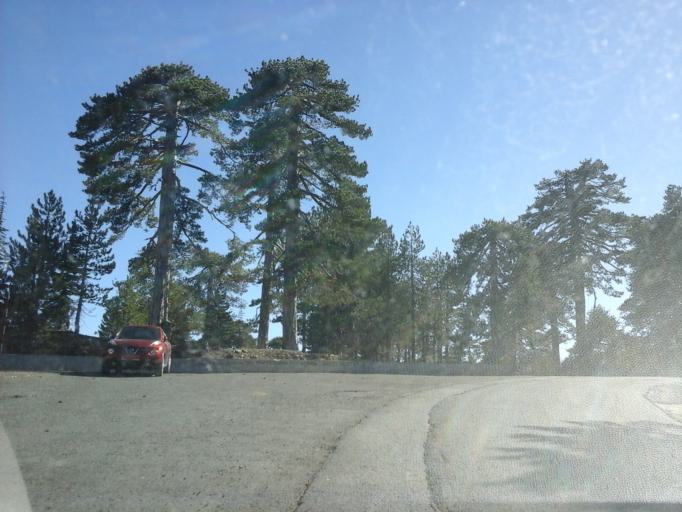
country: CY
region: Lefkosia
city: Kakopetria
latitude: 34.9318
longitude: 32.8709
